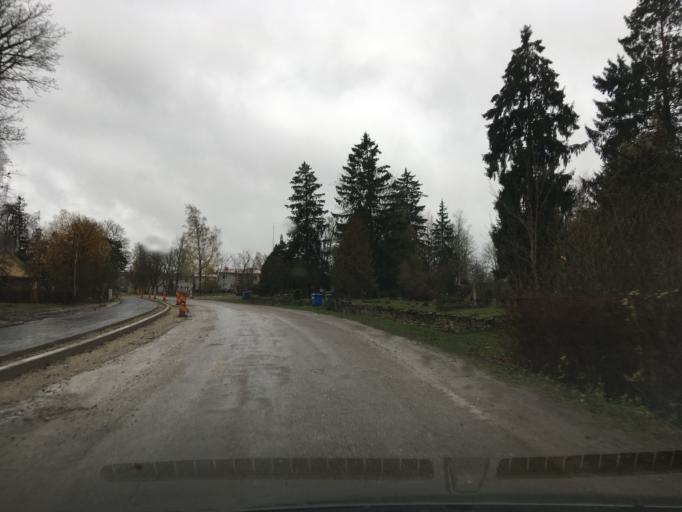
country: EE
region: Laeaene
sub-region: Lihula vald
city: Lihula
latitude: 58.6800
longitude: 23.8235
